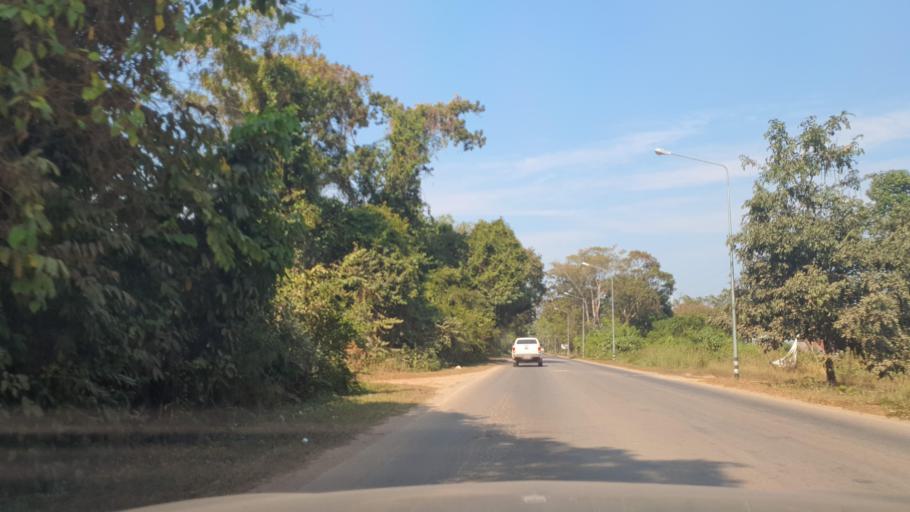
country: TH
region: Nakhon Phanom
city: Ban Phaeng
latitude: 18.0139
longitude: 104.1570
